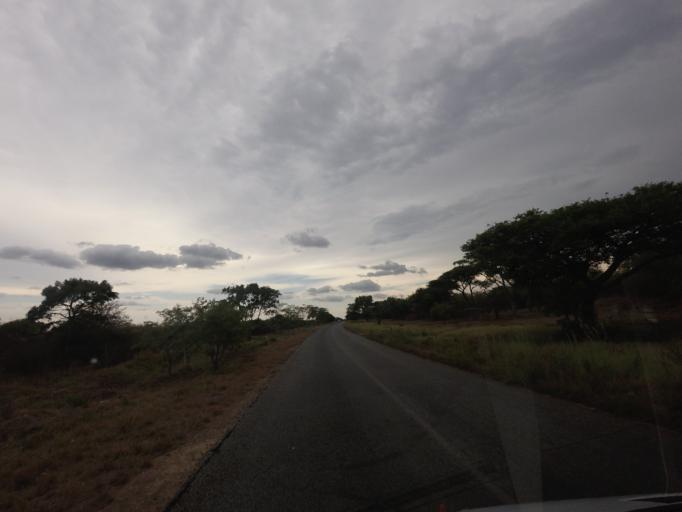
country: ZA
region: Limpopo
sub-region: Mopani District Municipality
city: Hoedspruit
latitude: -24.5091
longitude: 30.9388
